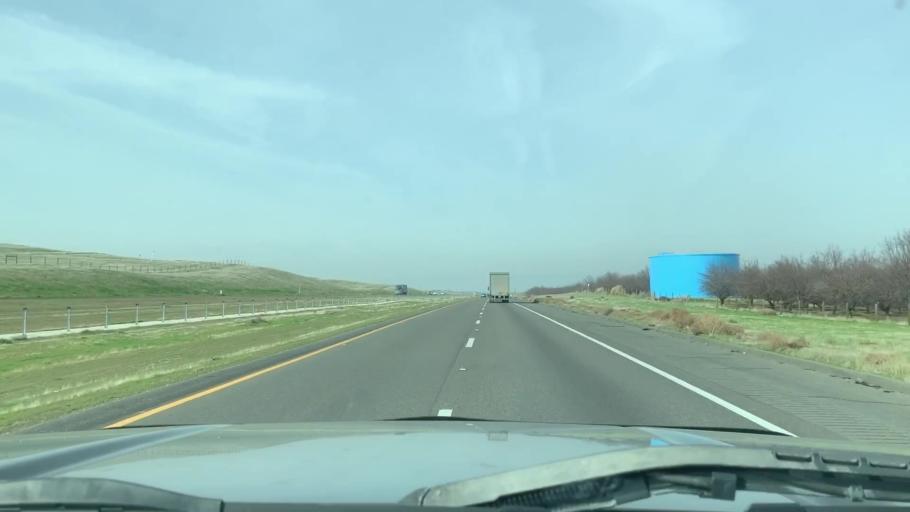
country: US
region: California
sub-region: Kings County
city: Avenal
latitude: 36.0576
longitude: -120.0699
